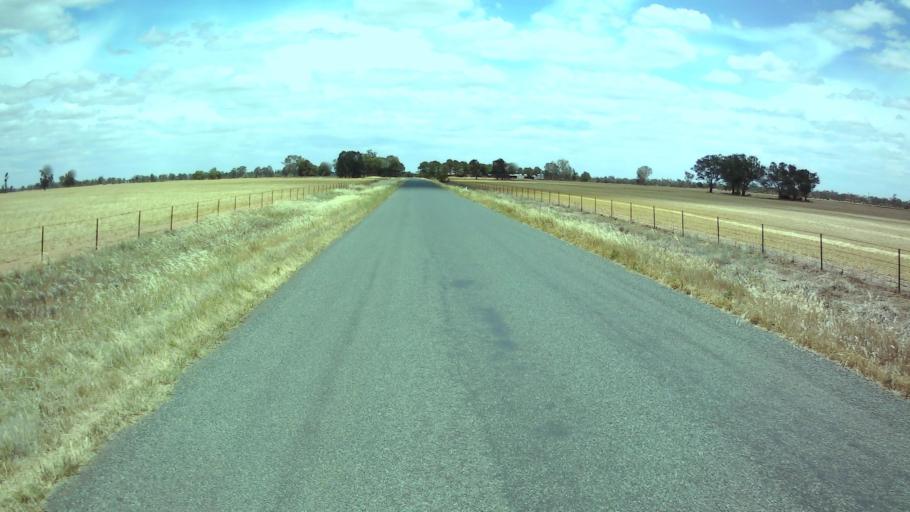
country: AU
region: New South Wales
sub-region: Weddin
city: Grenfell
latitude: -34.0425
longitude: 147.7870
